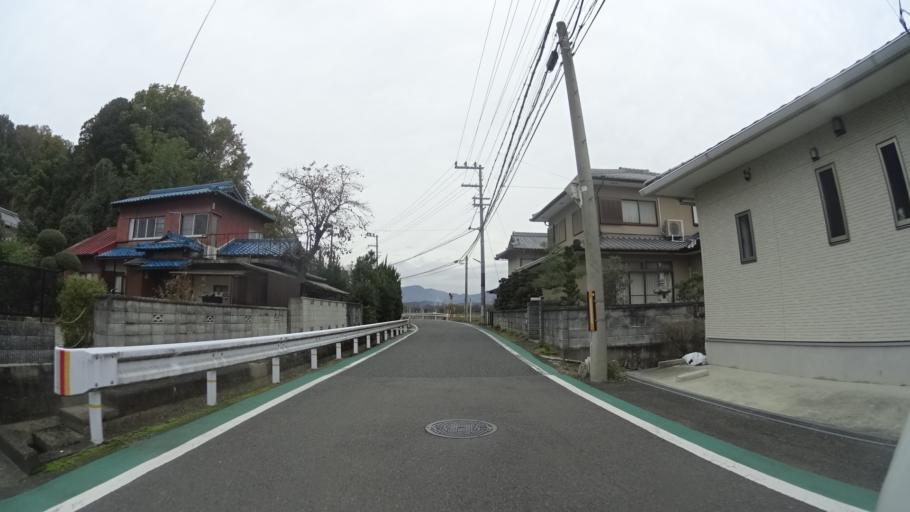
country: JP
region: Kyoto
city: Kameoka
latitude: 35.0547
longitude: 135.5457
